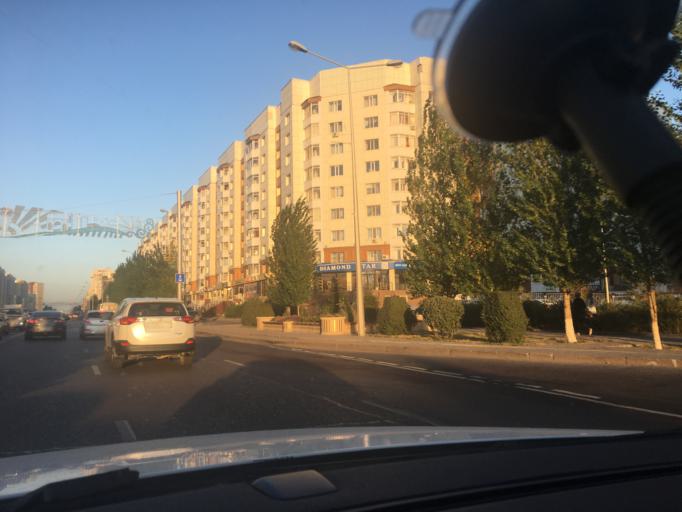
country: KZ
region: Astana Qalasy
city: Astana
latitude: 51.1370
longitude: 71.4679
